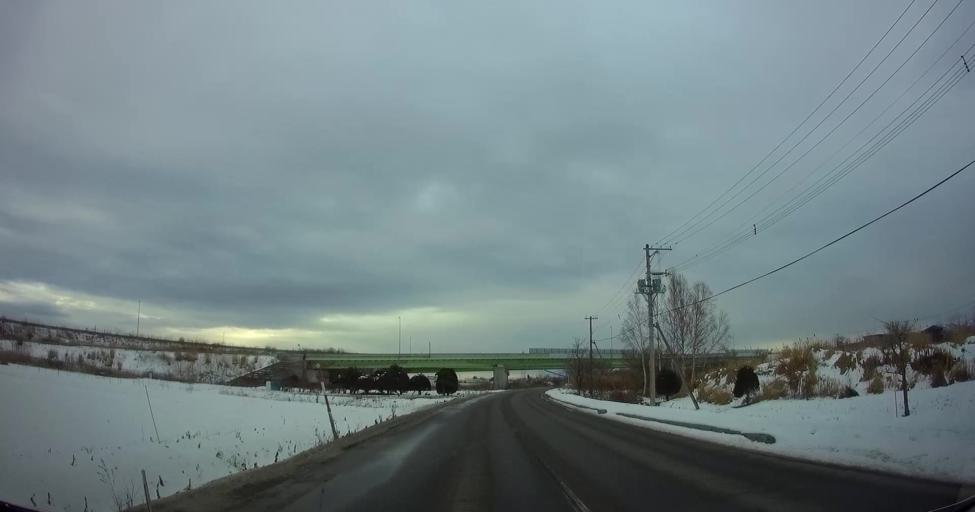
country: JP
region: Hokkaido
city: Nanae
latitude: 41.8356
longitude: 140.6912
